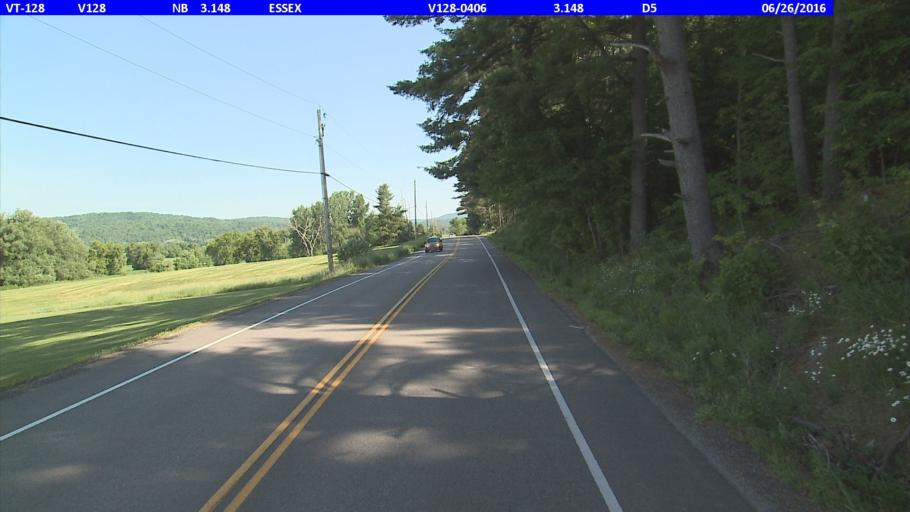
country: US
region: Vermont
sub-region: Chittenden County
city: Jericho
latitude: 44.5429
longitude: -73.0329
